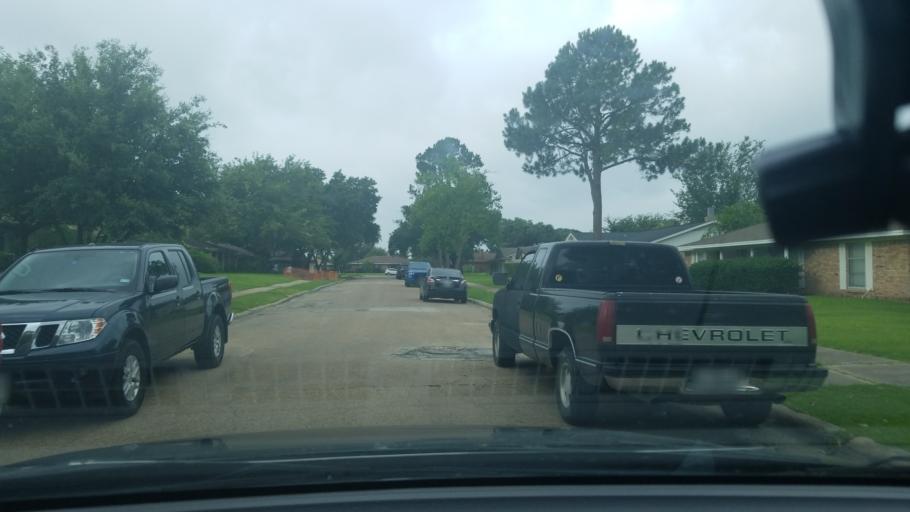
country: US
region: Texas
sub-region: Dallas County
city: Mesquite
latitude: 32.7823
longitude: -96.6381
